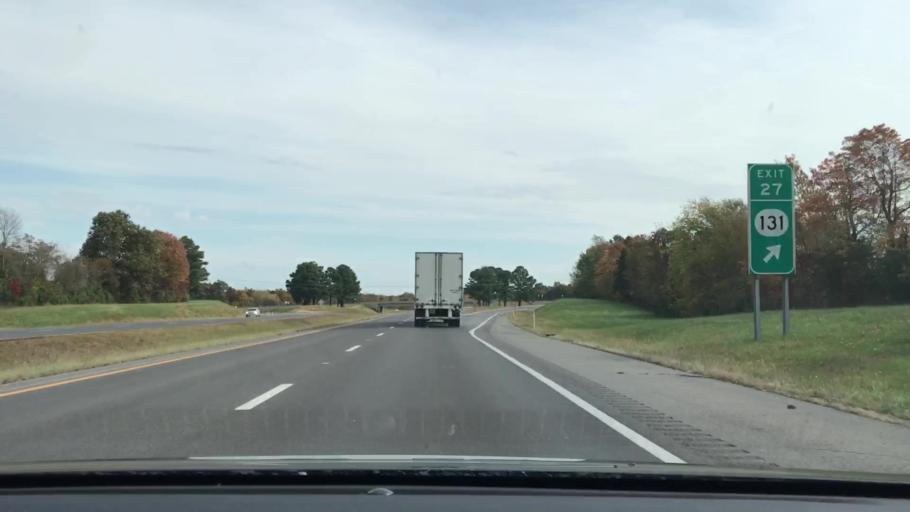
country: US
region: Kentucky
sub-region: Graves County
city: Mayfield
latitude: 36.7739
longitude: -88.6001
